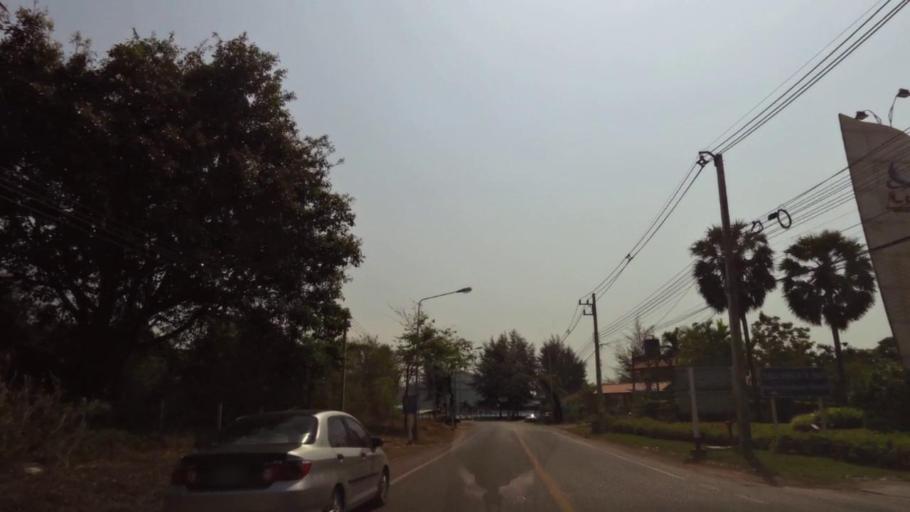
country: TH
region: Chanthaburi
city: Tha Mai
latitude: 12.5340
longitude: 101.9420
